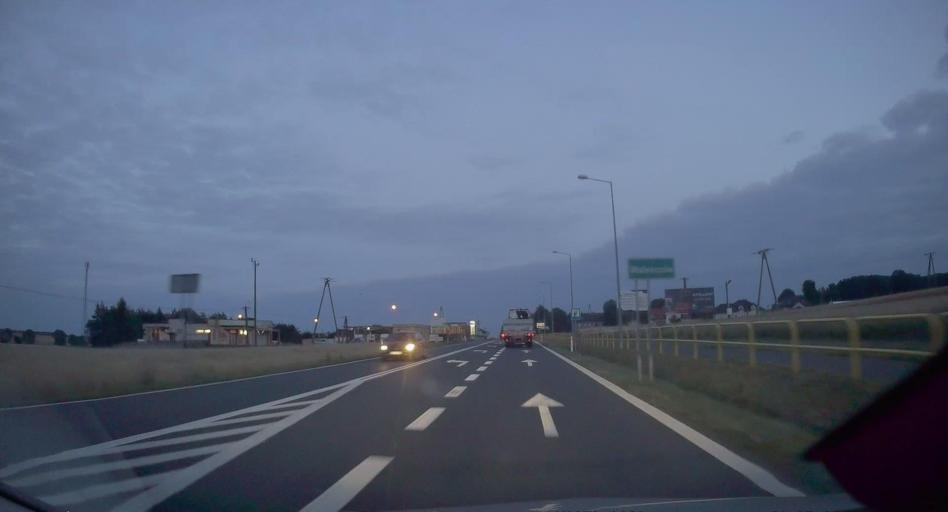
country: PL
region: Silesian Voivodeship
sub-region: Powiat klobucki
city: Opatow
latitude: 50.9310
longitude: 18.8577
